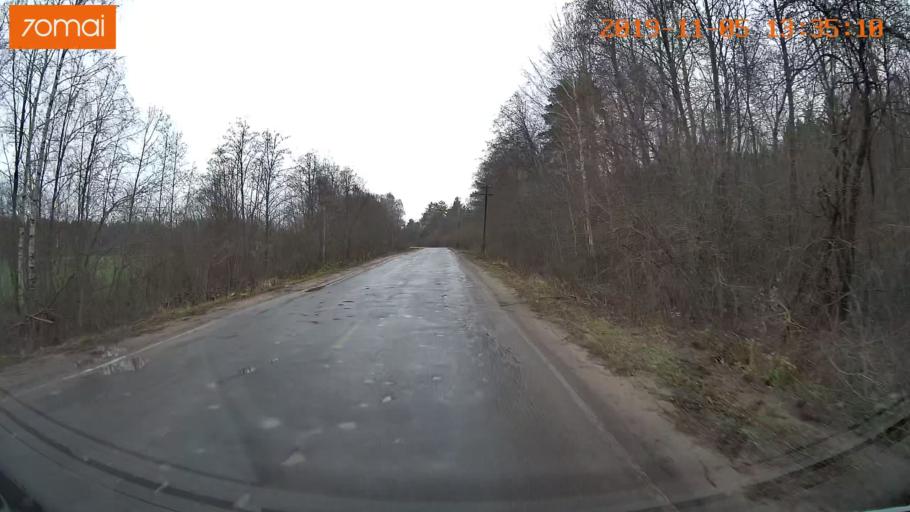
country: RU
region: Ivanovo
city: Shuya
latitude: 56.9059
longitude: 41.3885
